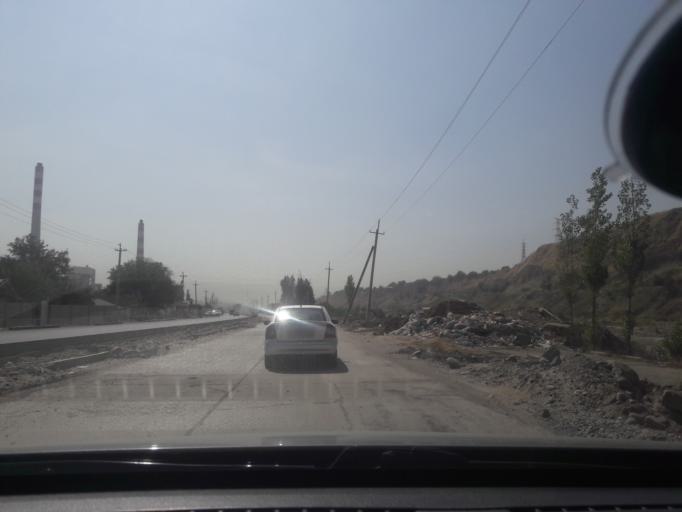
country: TJ
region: Dushanbe
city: Dushanbe
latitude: 38.6172
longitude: 68.7683
